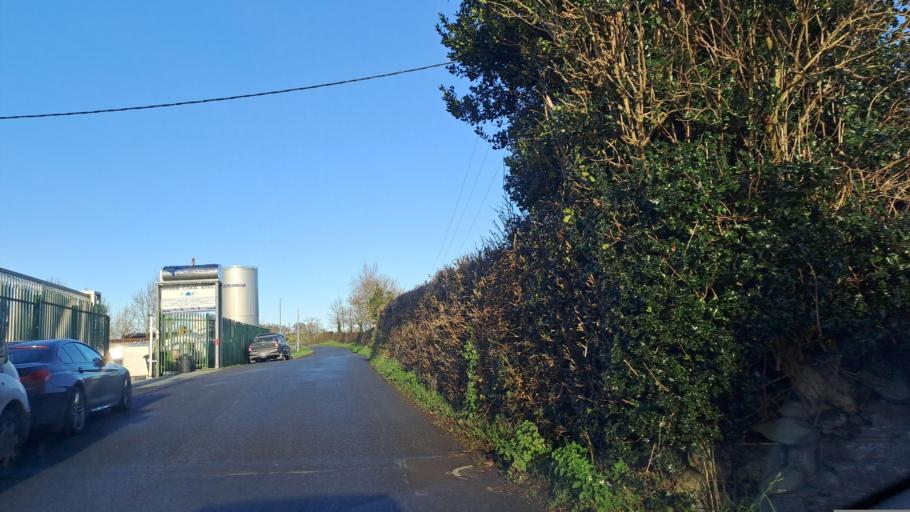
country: IE
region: Ulster
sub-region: An Cabhan
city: Mullagh
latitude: 53.8118
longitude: -6.9442
